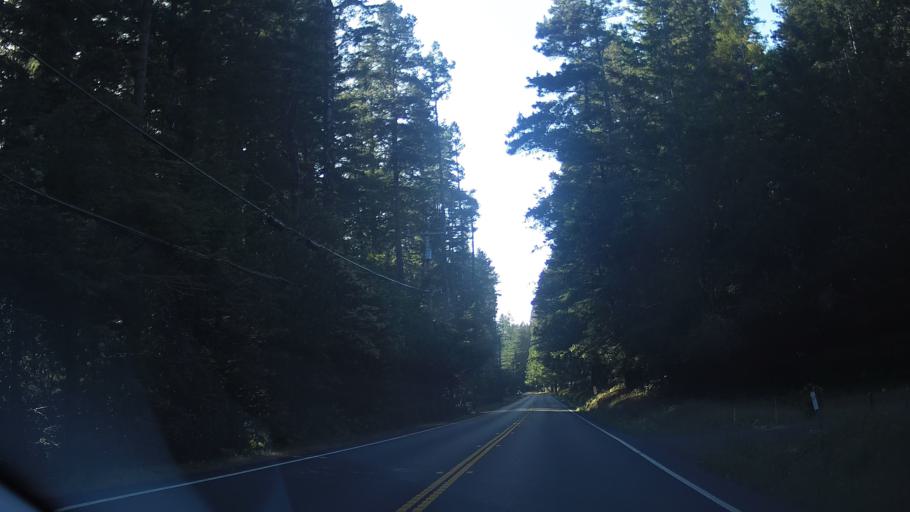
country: US
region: California
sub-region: Mendocino County
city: Fort Bragg
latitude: 39.4034
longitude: -123.7401
